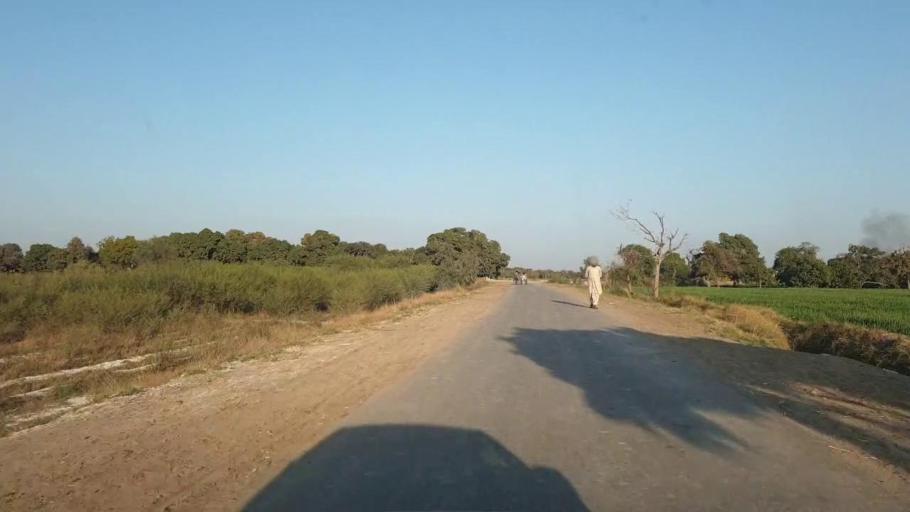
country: PK
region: Sindh
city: Tando Allahyar
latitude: 25.3539
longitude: 68.7190
